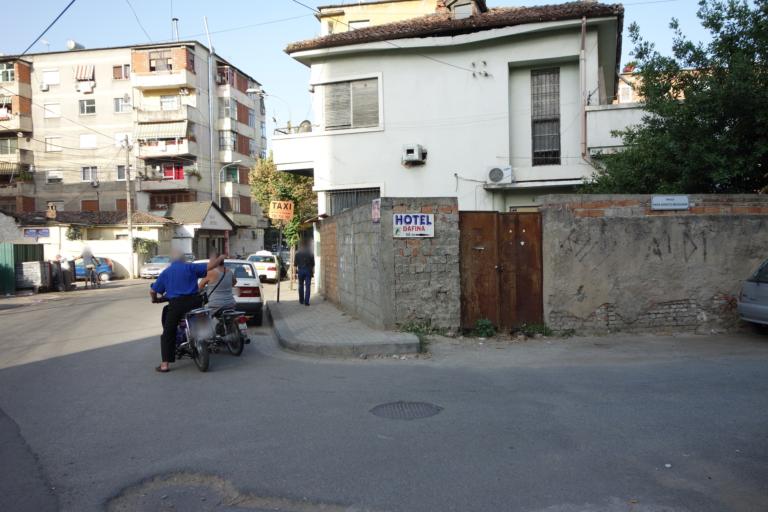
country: AL
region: Tirane
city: Tirana
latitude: 41.3335
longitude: 19.8180
